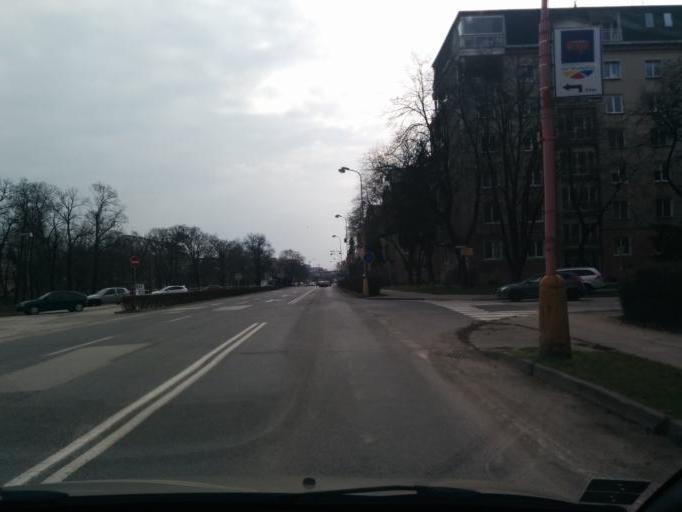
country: SK
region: Trnavsky
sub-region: Okres Trnava
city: Trnava
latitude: 48.3743
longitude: 17.5831
